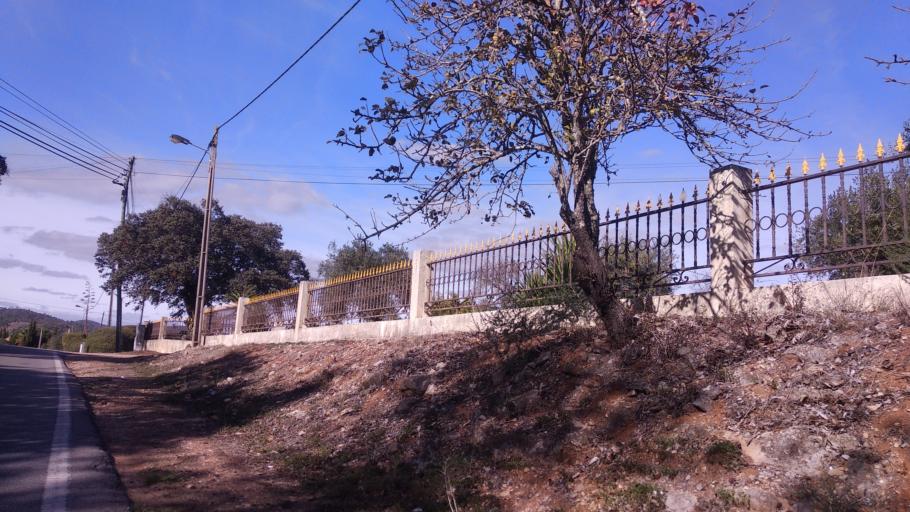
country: PT
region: Faro
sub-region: Sao Bras de Alportel
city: Sao Bras de Alportel
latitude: 37.1617
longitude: -7.9000
